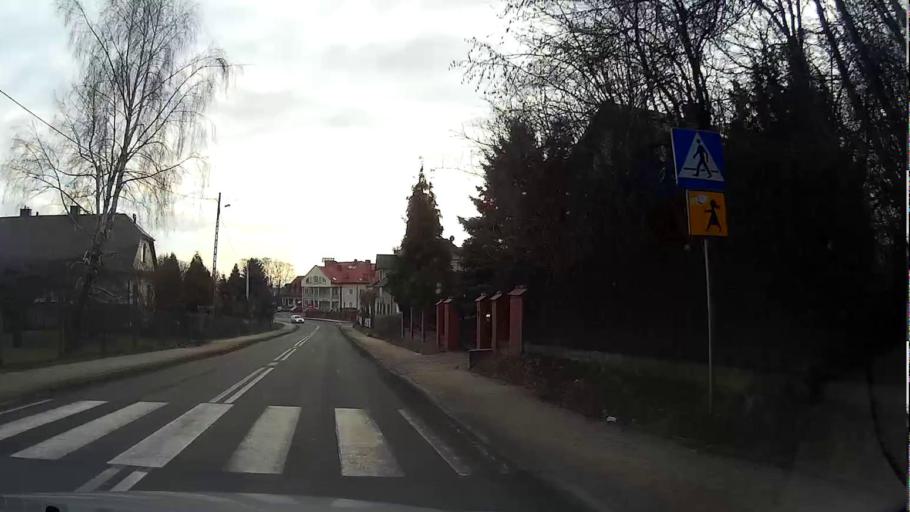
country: PL
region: Lesser Poland Voivodeship
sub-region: Powiat chrzanowski
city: Alwernia
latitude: 50.0682
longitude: 19.5422
